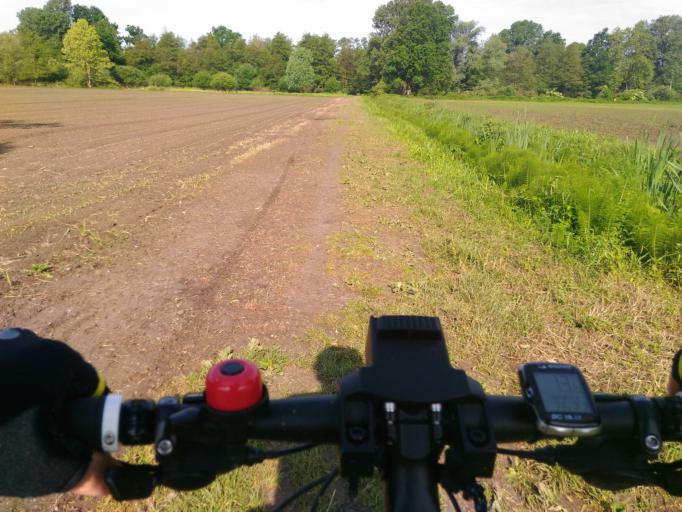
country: IT
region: Lombardy
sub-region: Provincia di Lodi
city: Lodi
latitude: 45.3124
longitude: 9.4824
